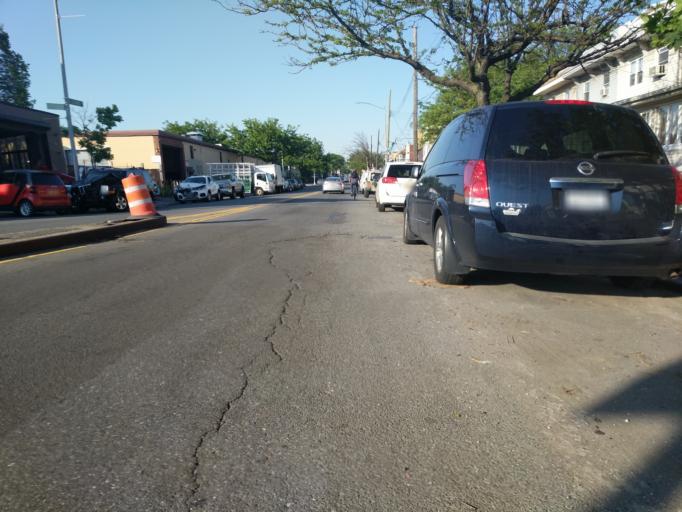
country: US
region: New York
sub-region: Queens County
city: Long Island City
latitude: 40.7189
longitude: -73.9075
